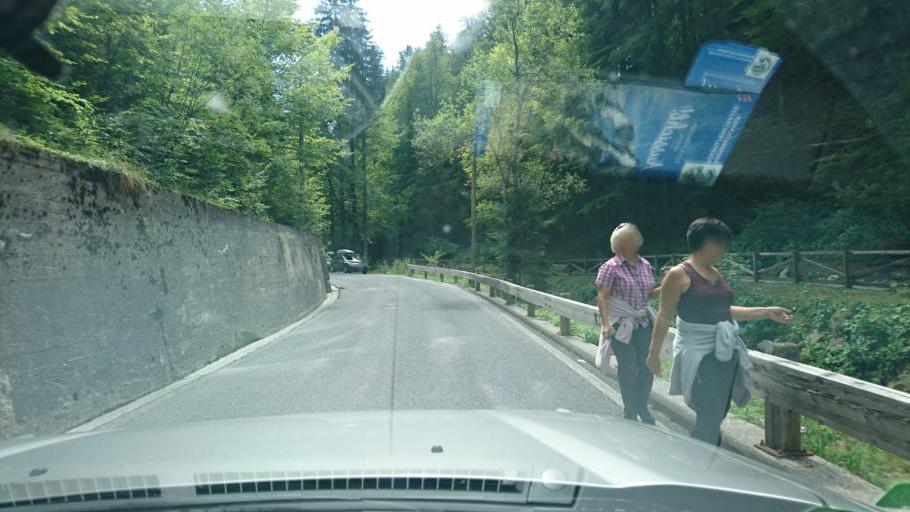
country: AT
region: Carinthia
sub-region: Politischer Bezirk Villach Land
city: Arnoldstein
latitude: 46.4847
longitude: 13.6744
